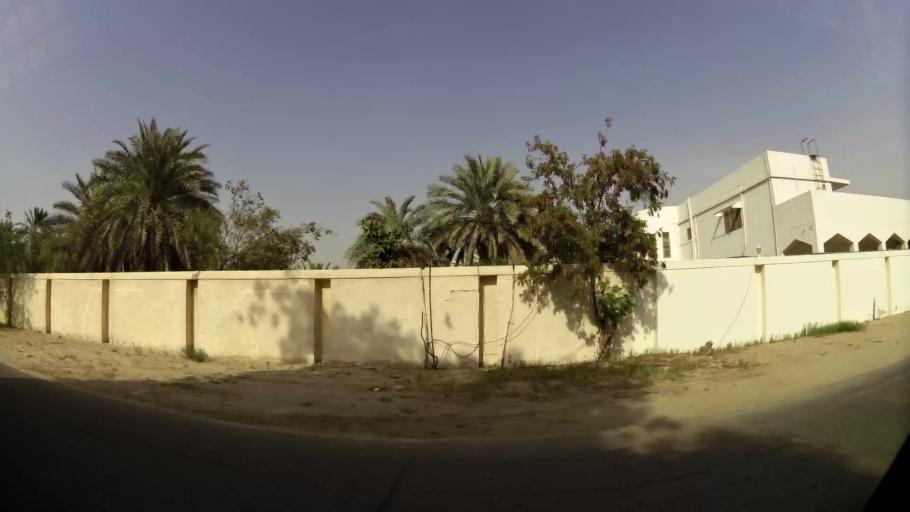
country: AE
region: Ash Shariqah
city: Sharjah
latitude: 25.2509
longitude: 55.4196
